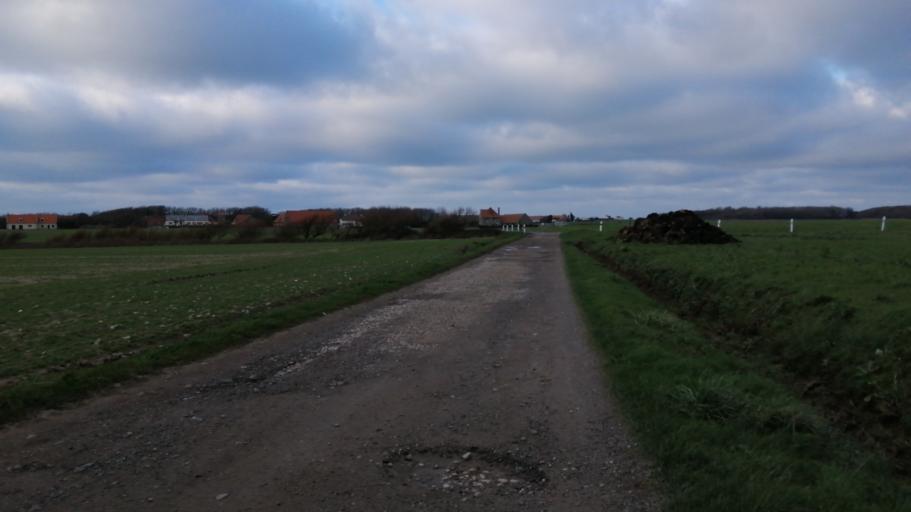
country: FR
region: Nord-Pas-de-Calais
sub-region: Departement du Pas-de-Calais
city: Ambleteuse
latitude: 50.8508
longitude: 1.5958
